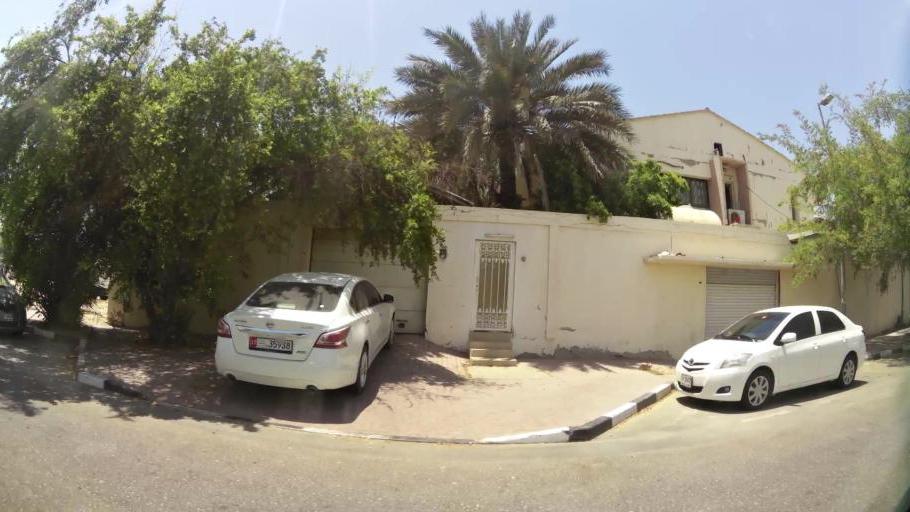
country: AE
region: Ash Shariqah
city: Sharjah
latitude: 25.2957
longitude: 55.3359
